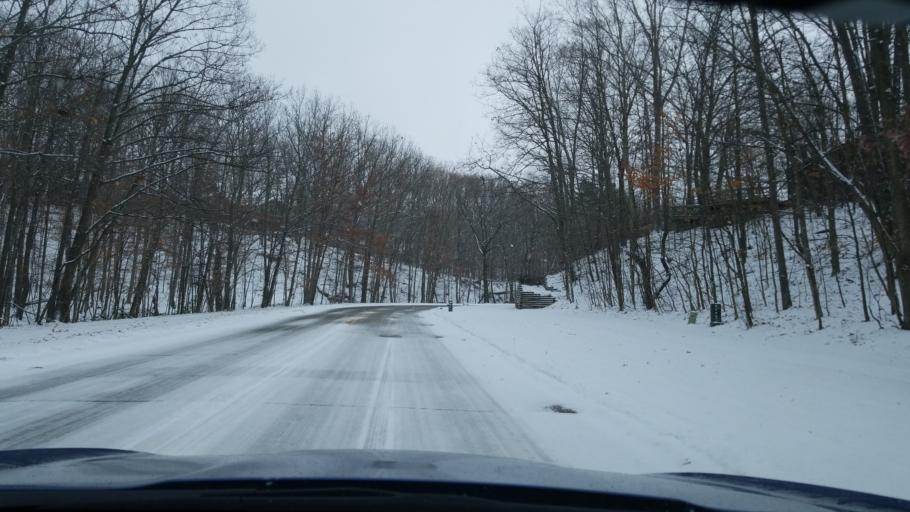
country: US
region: Ohio
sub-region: Cuyahoga County
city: Strongsville
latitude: 41.3231
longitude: -81.8259
